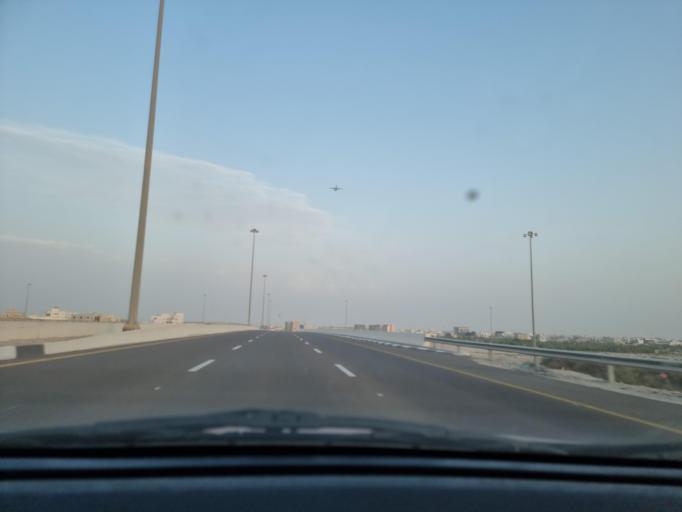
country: AE
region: Abu Dhabi
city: Abu Dhabi
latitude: 24.3780
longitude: 54.7316
